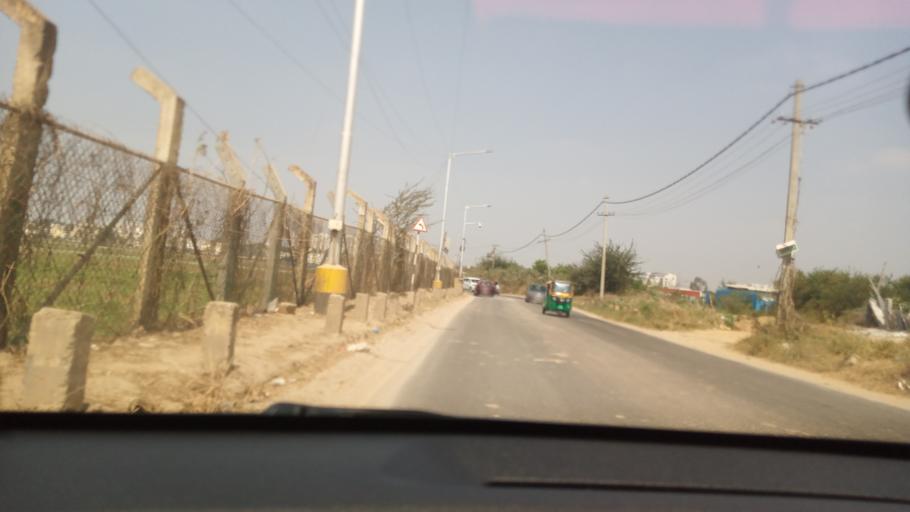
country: IN
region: Karnataka
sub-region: Bangalore Rural
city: Hoskote
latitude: 12.9482
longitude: 77.7457
